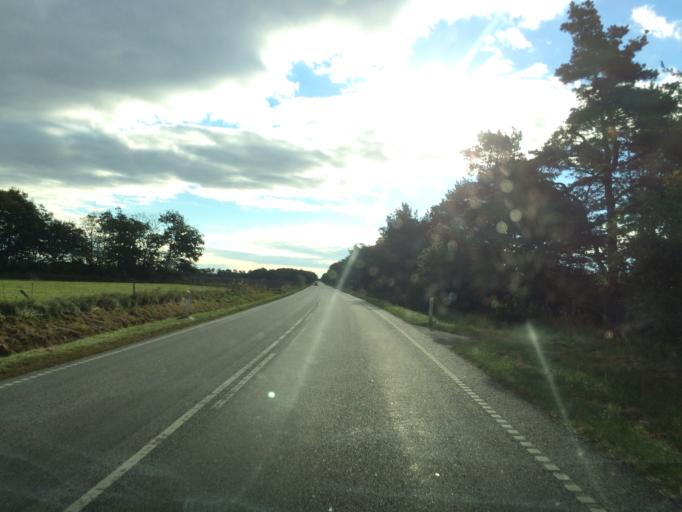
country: DK
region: Central Jutland
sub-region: Herning Kommune
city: Kibaek
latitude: 55.9490
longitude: 8.7417
